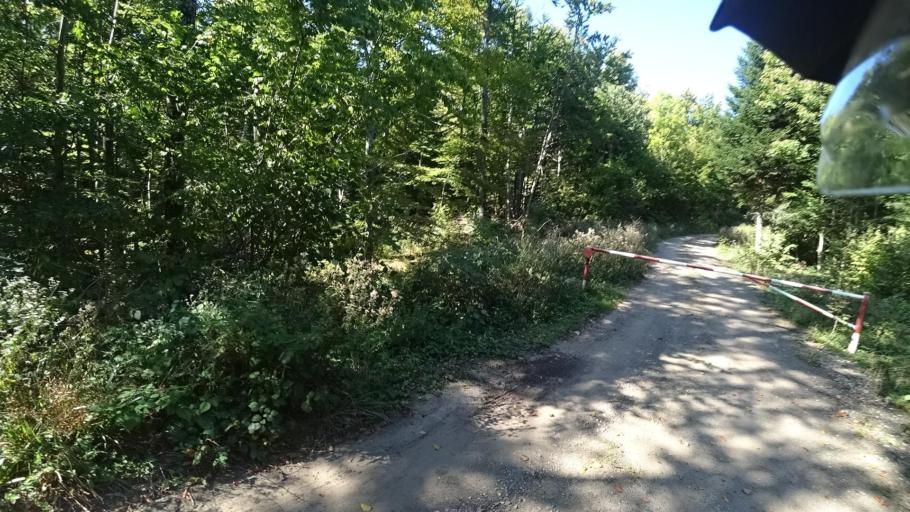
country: HR
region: Karlovacka
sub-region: Grad Ogulin
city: Ogulin
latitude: 45.2026
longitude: 15.1545
